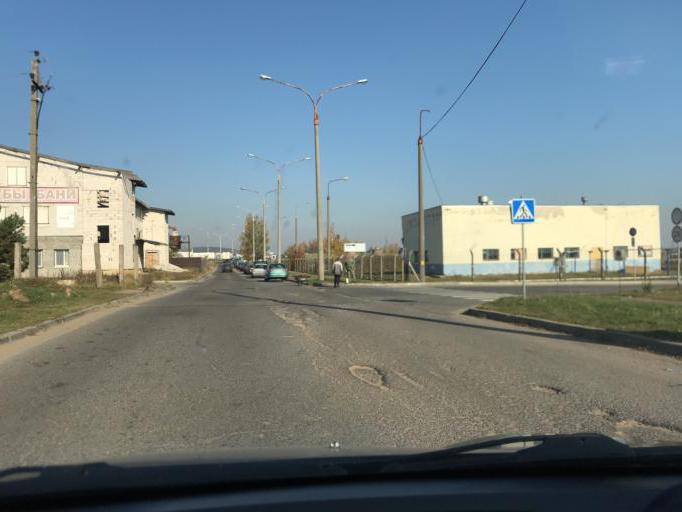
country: BY
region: Minsk
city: Pryvol'ny
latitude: 53.8123
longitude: 27.7849
